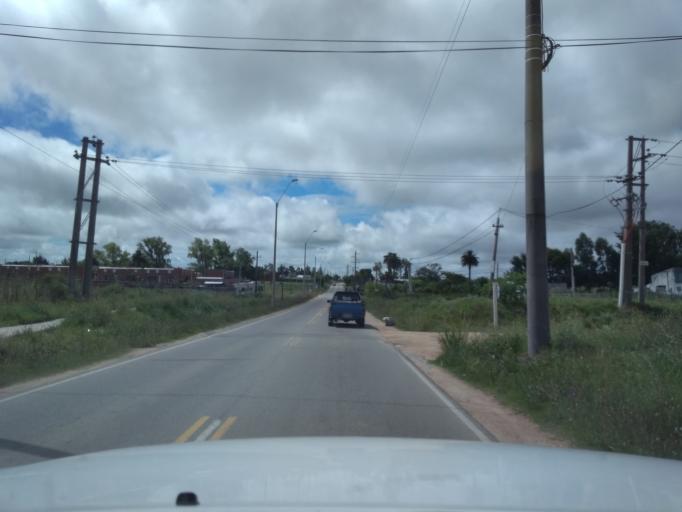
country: UY
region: Canelones
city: Pando
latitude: -34.7091
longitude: -55.9646
